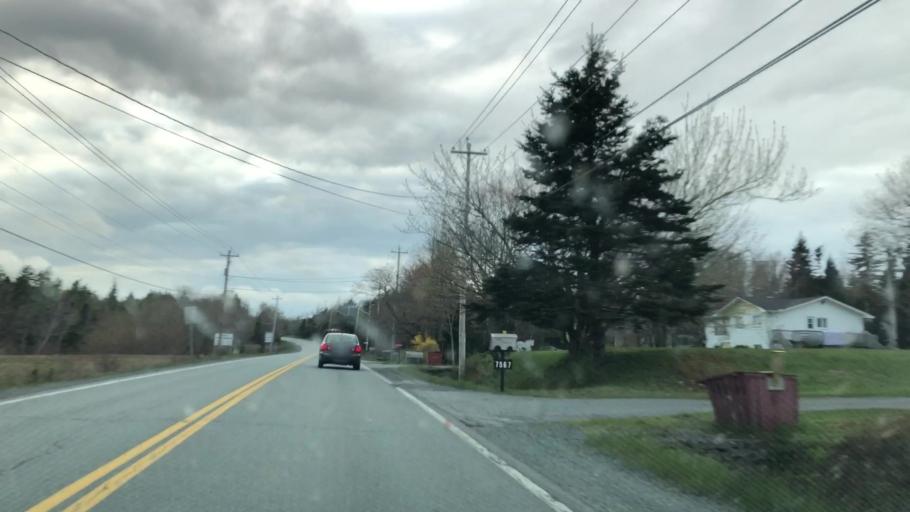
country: CA
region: Nova Scotia
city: Cole Harbour
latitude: 44.7835
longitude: -63.1670
